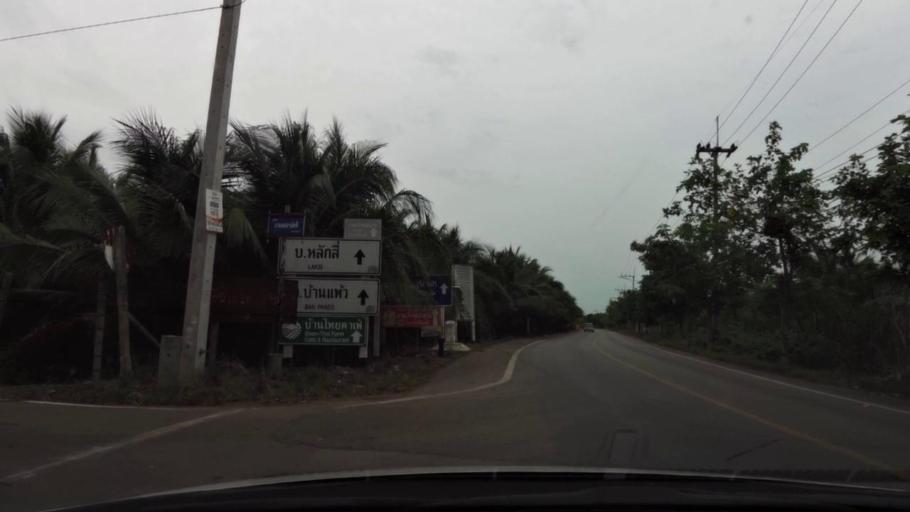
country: TH
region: Samut Sakhon
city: Ban Phaeo
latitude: 13.5834
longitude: 100.0369
